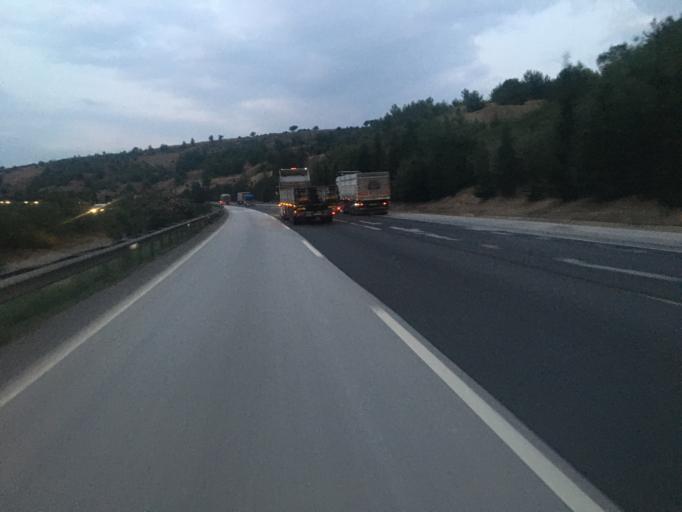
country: TR
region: Osmaniye
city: Haruniye
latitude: 37.1780
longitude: 36.3788
